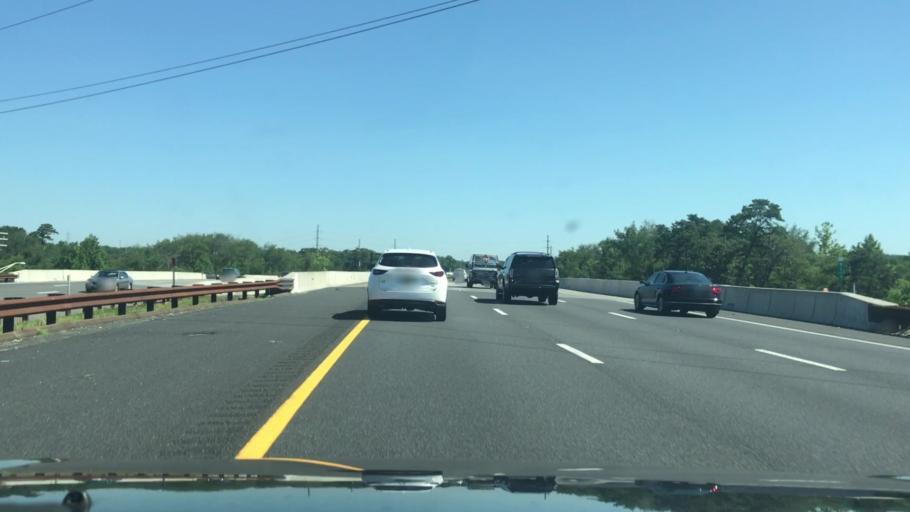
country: US
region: New Jersey
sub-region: Ocean County
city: Leisure Village
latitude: 40.0773
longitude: -74.1559
